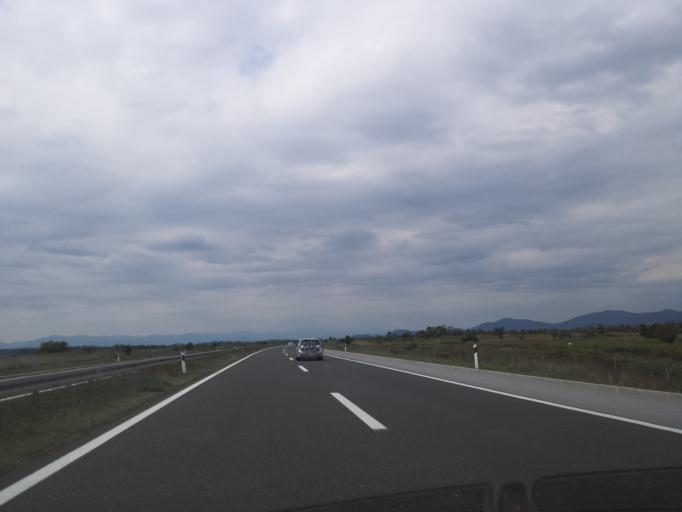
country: HR
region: Licko-Senjska
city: Gospic
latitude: 44.4826
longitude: 15.5554
